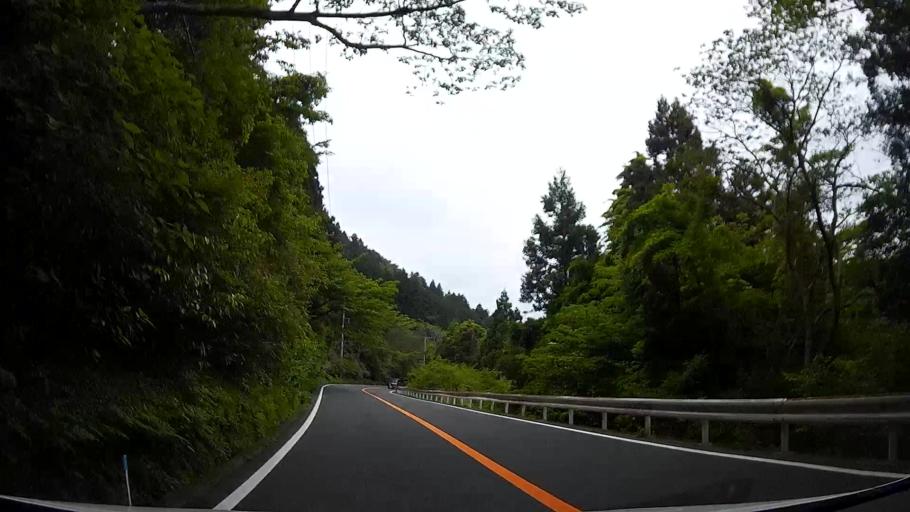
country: JP
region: Shizuoka
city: Ito
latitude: 34.9297
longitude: 139.0360
